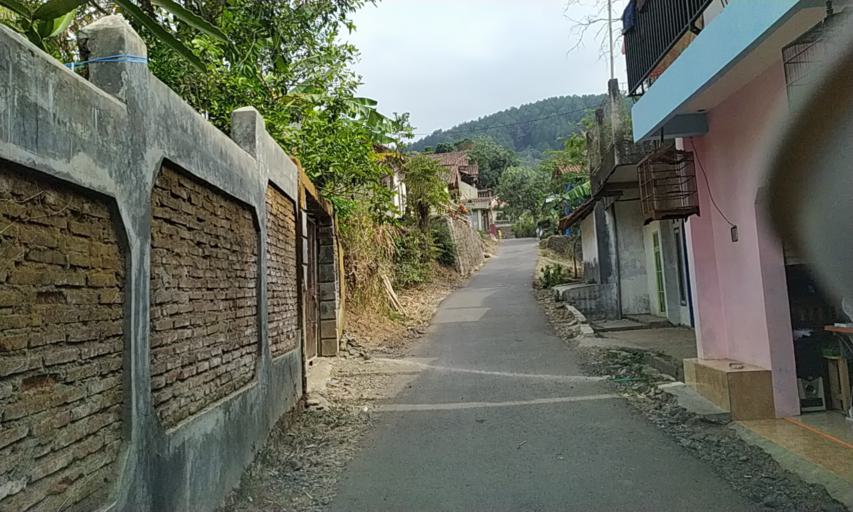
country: ID
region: Central Java
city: Telagasari
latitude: -7.3040
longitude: 108.8324
